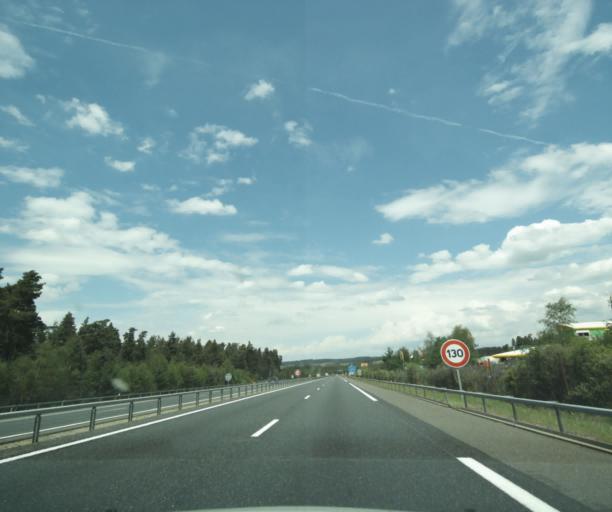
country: FR
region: Languedoc-Roussillon
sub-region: Departement de la Lozere
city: Aumont-Aubrac
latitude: 44.7381
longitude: 3.2891
